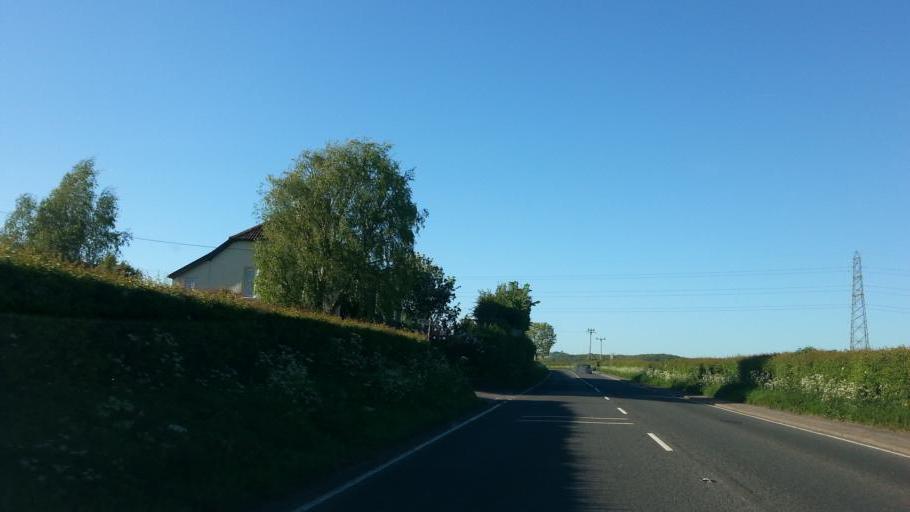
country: GB
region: England
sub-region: Bath and North East Somerset
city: Clutton
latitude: 51.3028
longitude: -2.5329
